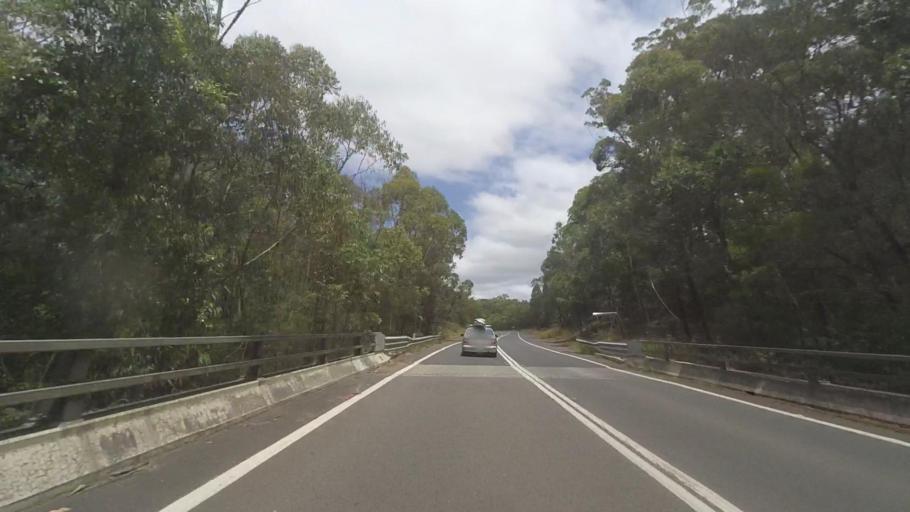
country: AU
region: New South Wales
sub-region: Shoalhaven Shire
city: Milton
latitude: -35.2401
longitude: 150.4294
